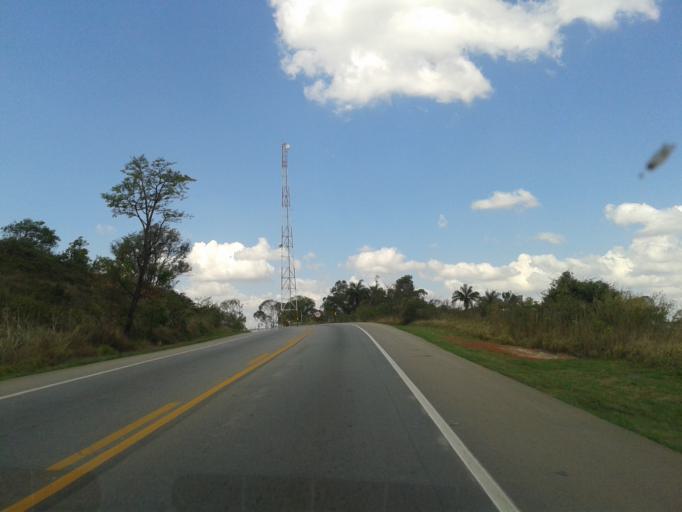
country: BR
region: Minas Gerais
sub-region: Campos Altos
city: Campos Altos
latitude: -19.7461
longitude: -45.9507
